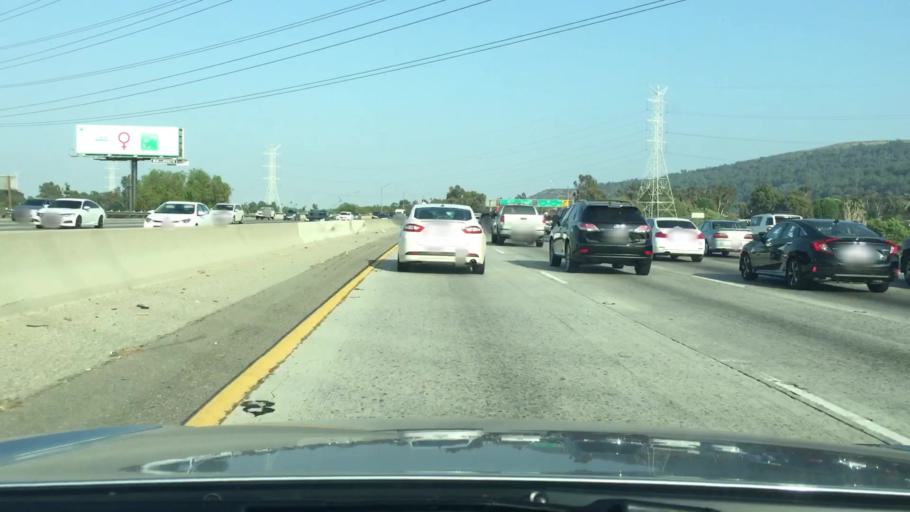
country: US
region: California
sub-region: Los Angeles County
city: South El Monte
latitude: 34.0372
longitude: -118.0345
